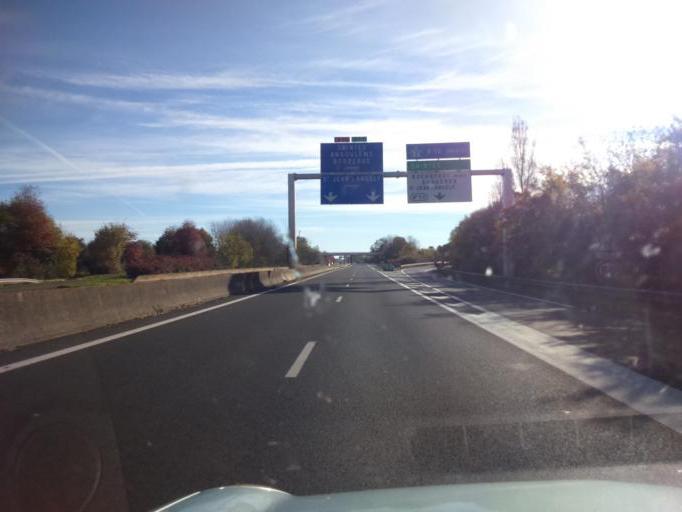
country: FR
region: Poitou-Charentes
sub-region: Departement de la Charente-Maritime
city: Breuil-Magne
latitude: 45.9627
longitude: -0.9615
